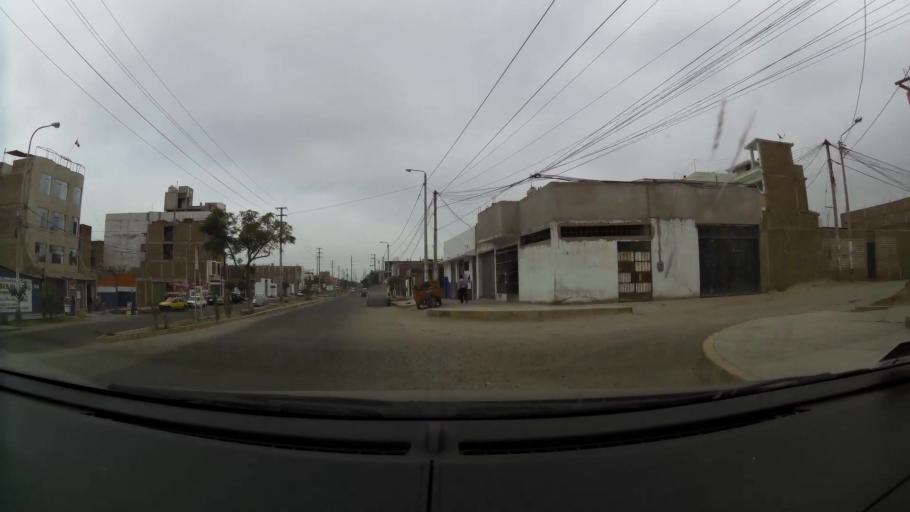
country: PE
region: La Libertad
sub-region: Provincia de Trujillo
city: La Esperanza
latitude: -8.0909
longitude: -79.0443
